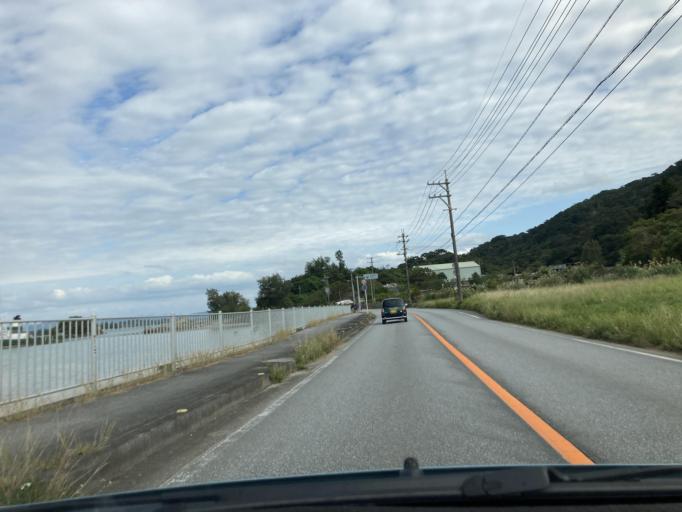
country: JP
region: Okinawa
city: Nago
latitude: 26.6467
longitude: 127.9877
